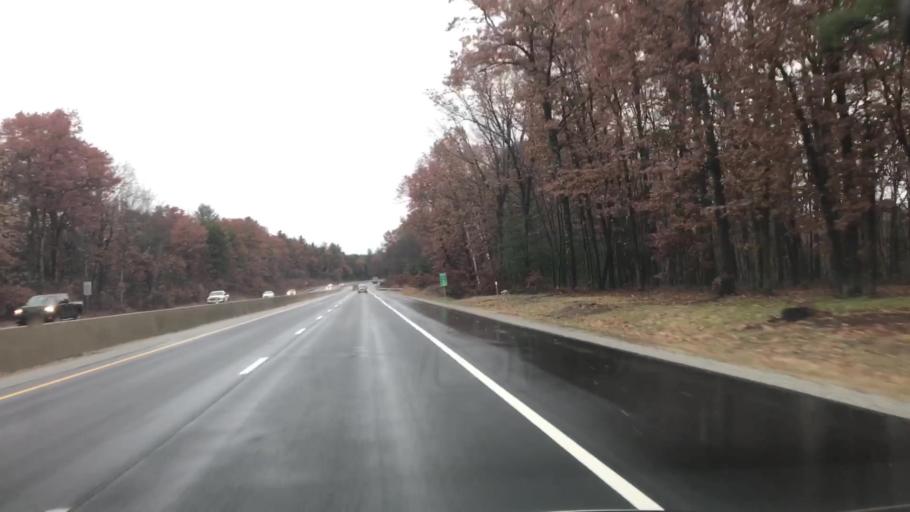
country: US
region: New Hampshire
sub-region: Hillsborough County
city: Pinardville
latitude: 43.0294
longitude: -71.4873
